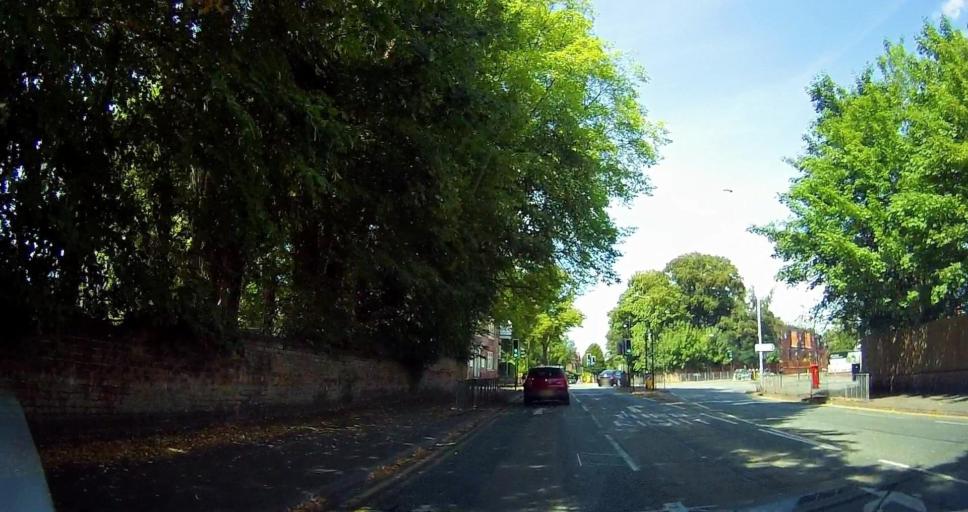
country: GB
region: England
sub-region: Wolverhampton
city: Wolverhampton
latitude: 52.5899
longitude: -2.1498
